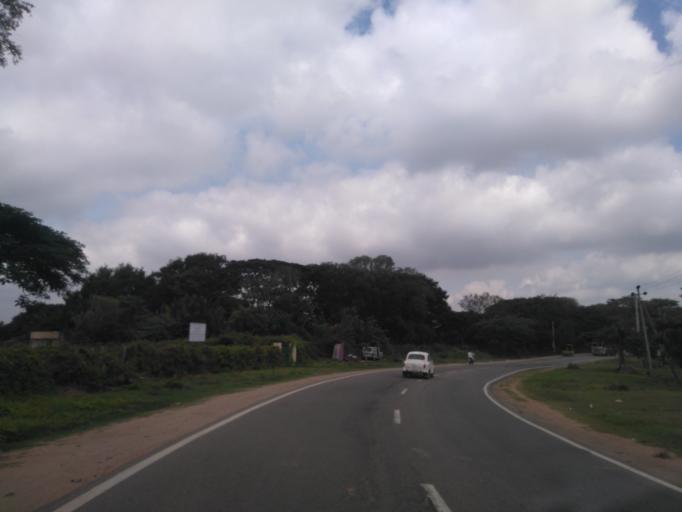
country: IN
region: Karnataka
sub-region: Mysore
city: Mysore
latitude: 12.2987
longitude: 76.6952
